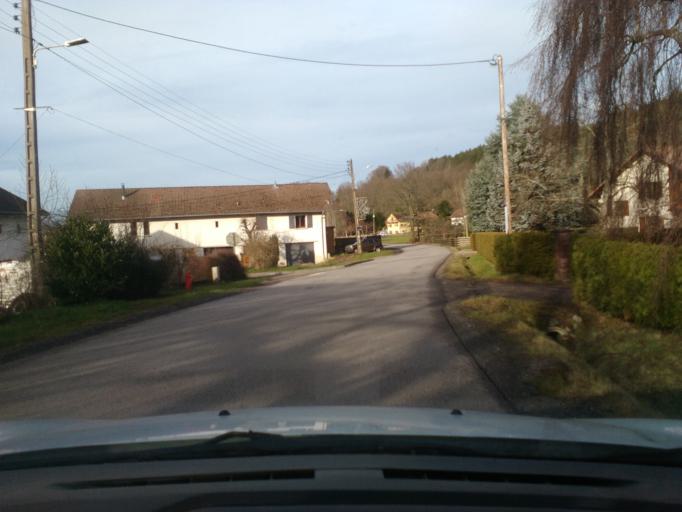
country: FR
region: Lorraine
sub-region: Departement des Vosges
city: Fraize
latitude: 48.1735
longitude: 6.9787
